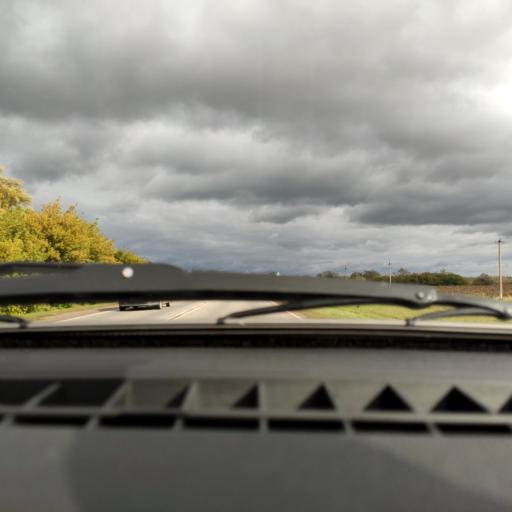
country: RU
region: Bashkortostan
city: Rayevskiy
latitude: 54.0134
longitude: 54.8691
